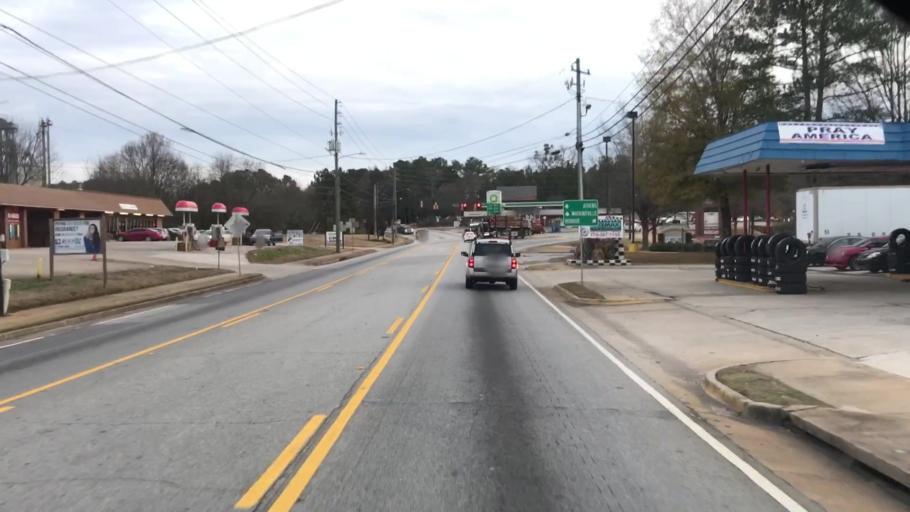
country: US
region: Georgia
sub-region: Barrow County
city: Winder
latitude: 33.9831
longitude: -83.7129
